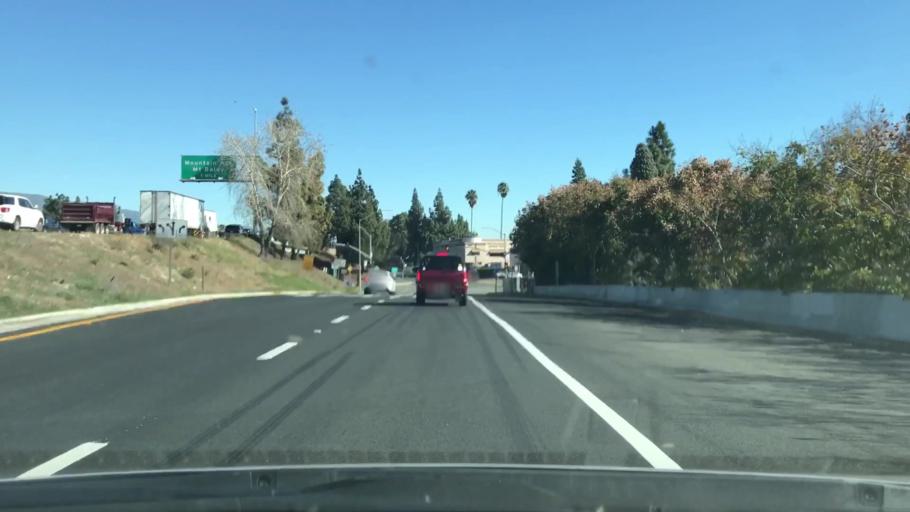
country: US
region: California
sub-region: San Bernardino County
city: Montclair
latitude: 34.0845
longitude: -117.6909
